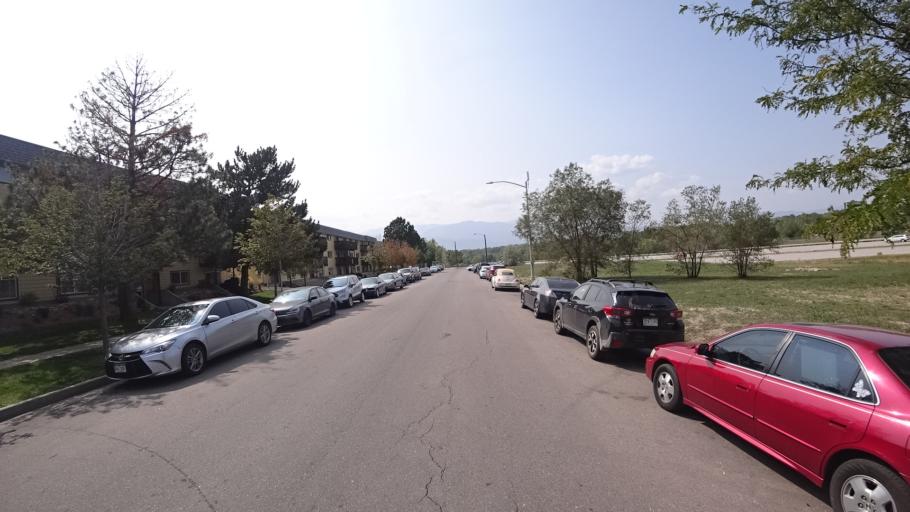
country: US
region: Colorado
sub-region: El Paso County
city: Stratmoor
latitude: 38.8155
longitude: -104.7832
